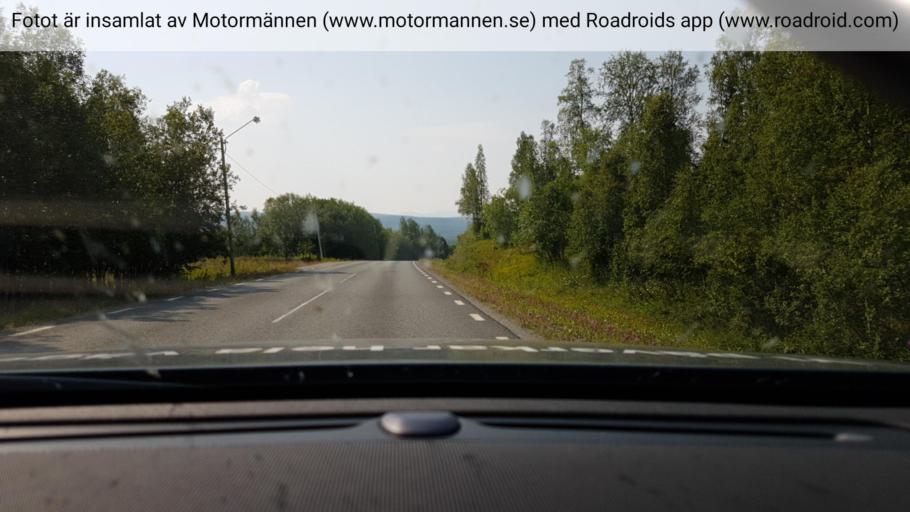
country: NO
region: Nordland
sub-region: Rana
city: Mo i Rana
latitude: 65.7558
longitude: 15.1125
